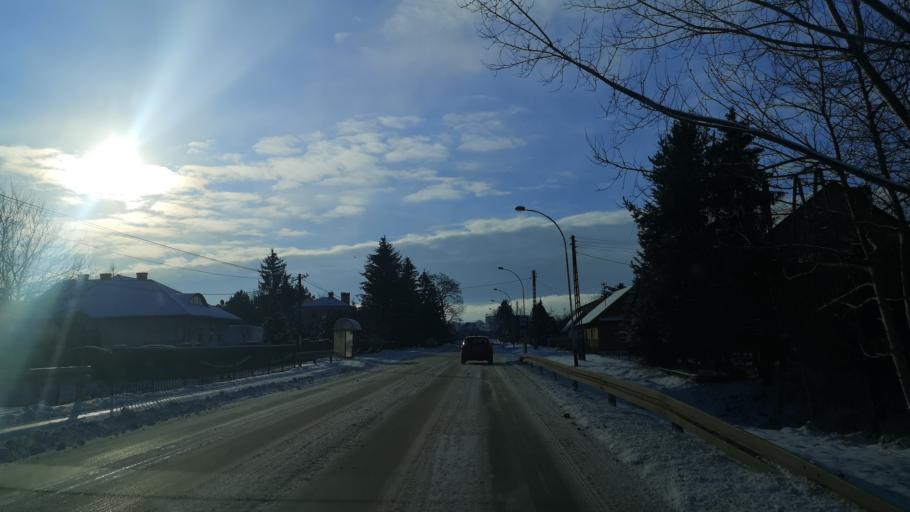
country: PL
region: Subcarpathian Voivodeship
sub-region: Powiat przeworski
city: Gorliczyna
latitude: 50.0773
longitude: 22.4935
